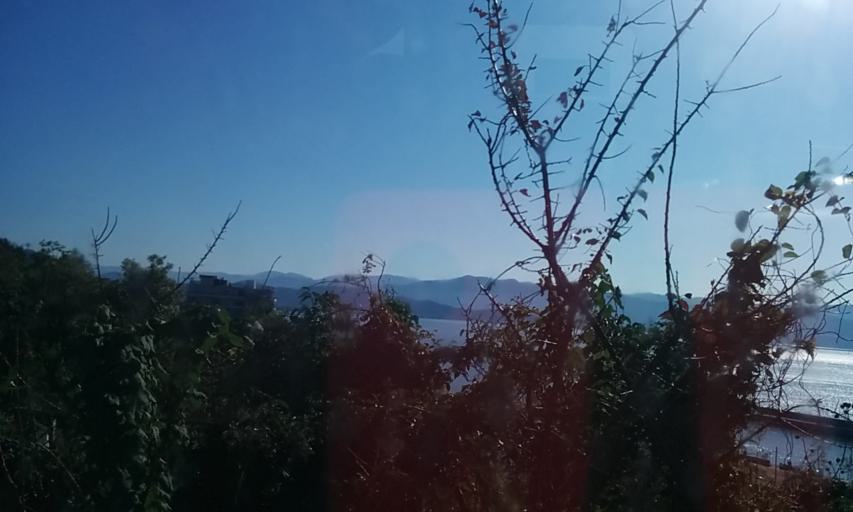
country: JP
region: Wakayama
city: Minato
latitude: 34.1853
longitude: 135.1509
